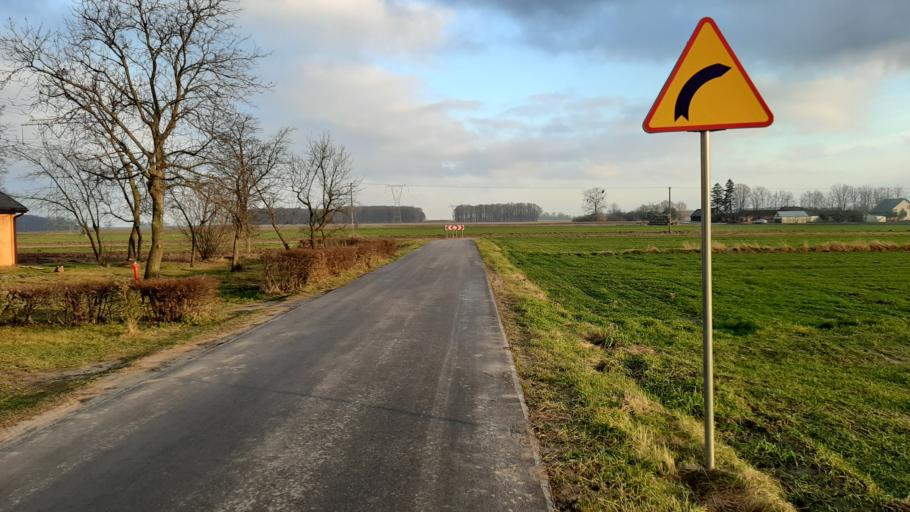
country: PL
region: Lublin Voivodeship
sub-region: Powiat lubelski
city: Jastkow
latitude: 51.3643
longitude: 22.4039
